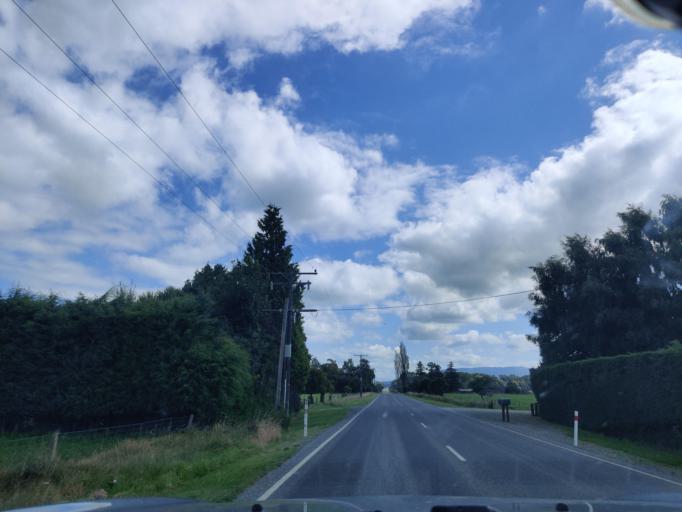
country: NZ
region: Canterbury
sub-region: Timaru District
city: Pleasant Point
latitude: -44.1266
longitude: 171.2708
